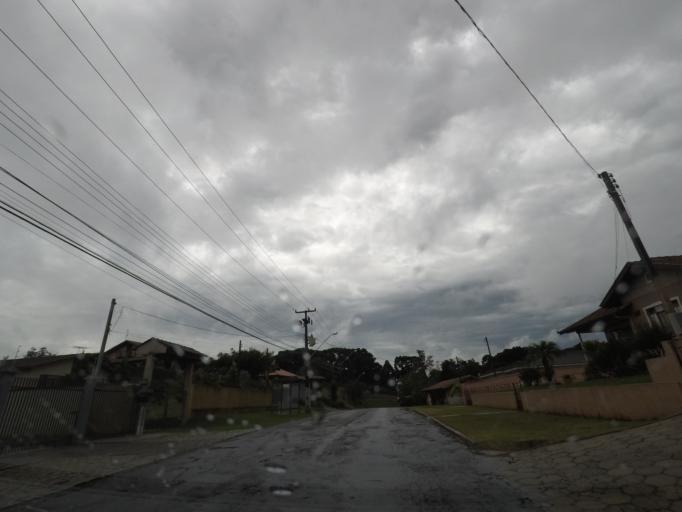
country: BR
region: Parana
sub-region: Campo Largo
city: Campo Largo
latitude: -25.4524
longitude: -49.4524
